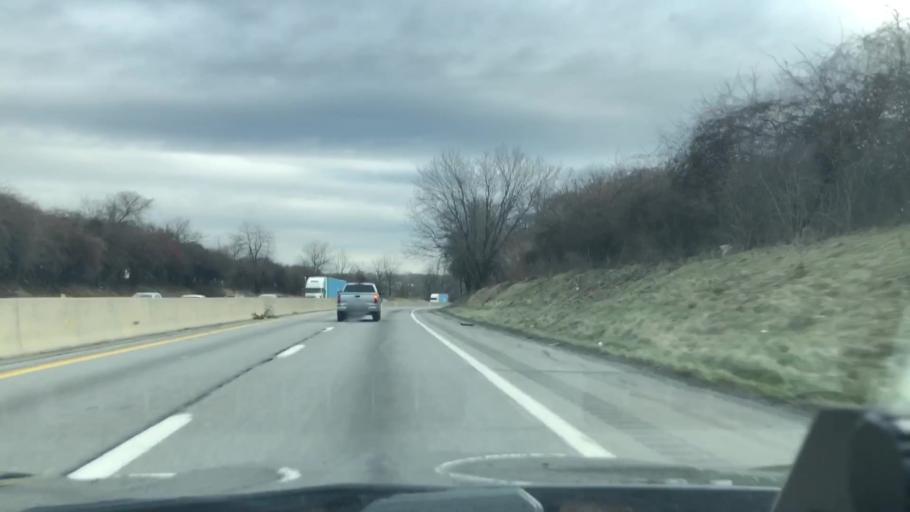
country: US
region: Pennsylvania
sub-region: Northampton County
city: Middletown
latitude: 40.6755
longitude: -75.3578
